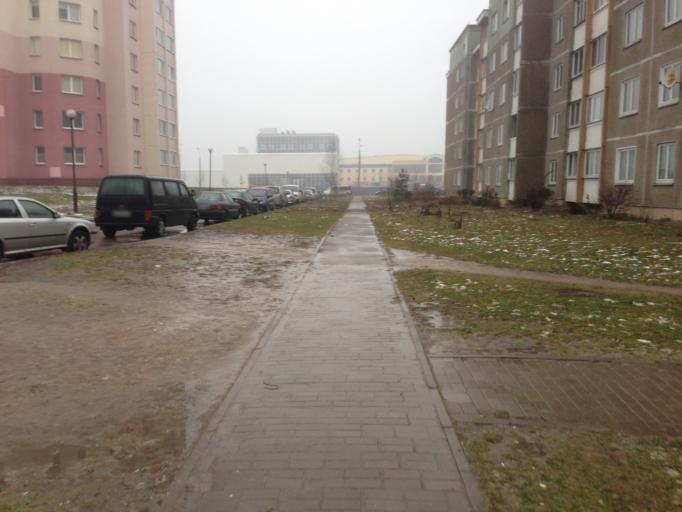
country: BY
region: Grodnenskaya
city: Hrodna
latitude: 53.7138
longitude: 23.8421
